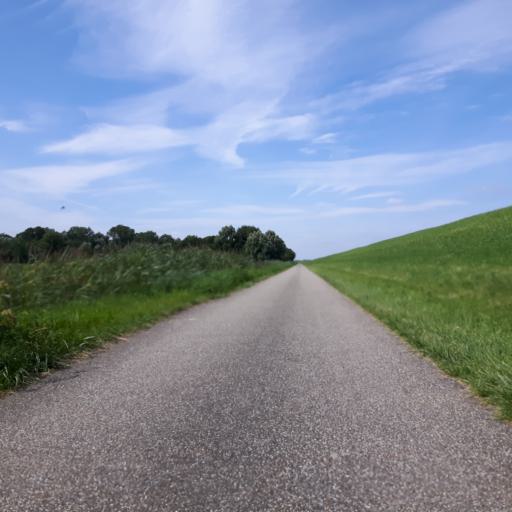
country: NL
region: Zeeland
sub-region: Schouwen-Duiveland
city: Bruinisse
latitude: 51.6491
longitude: 4.1429
